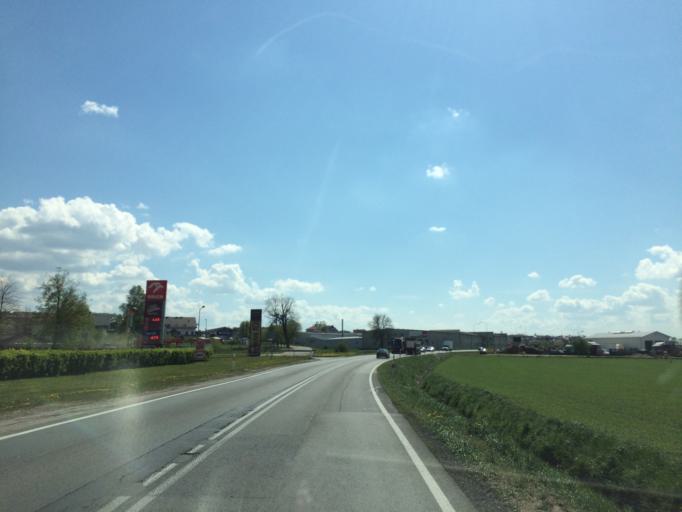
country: PL
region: Warmian-Masurian Voivodeship
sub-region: Powiat ilawski
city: Lubawa
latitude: 53.5135
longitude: 19.7452
